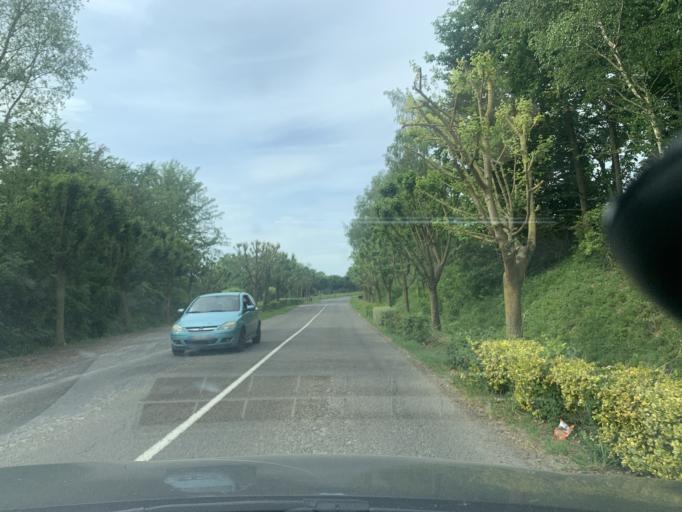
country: FR
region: Nord-Pas-de-Calais
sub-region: Departement du Nord
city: Marcoing
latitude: 50.1266
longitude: 3.1788
